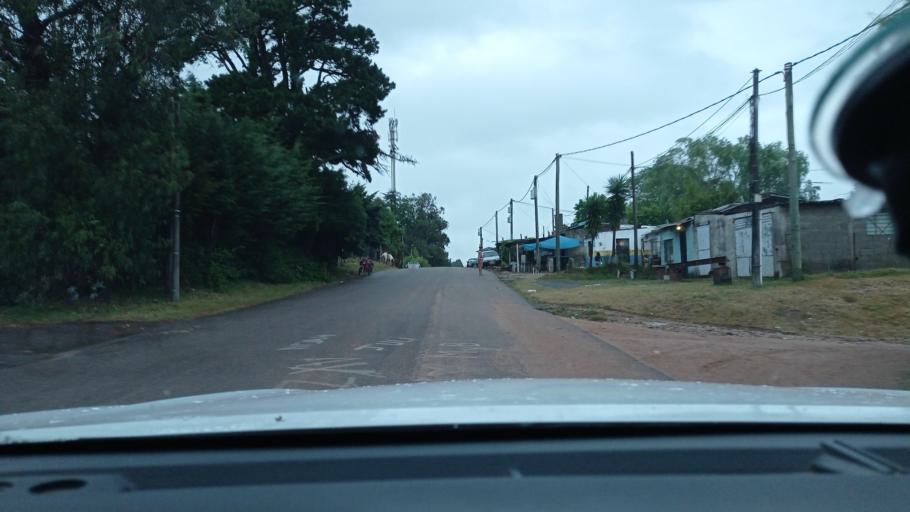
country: UY
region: Maldonado
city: Maldonado
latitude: -34.9220
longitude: -54.9120
